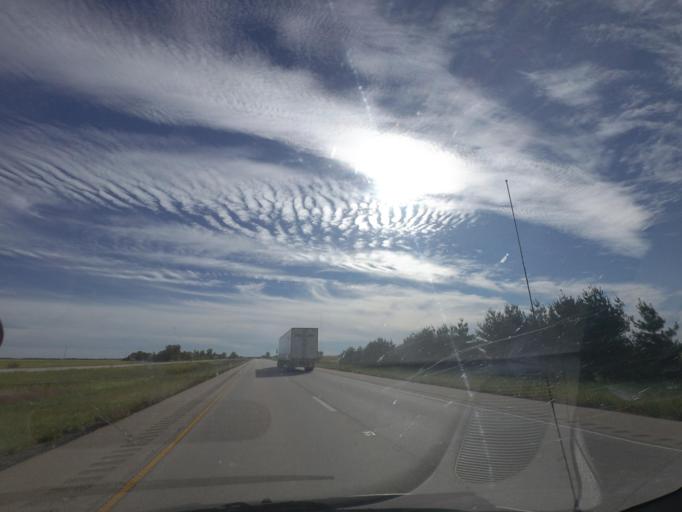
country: US
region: Illinois
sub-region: Piatt County
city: Cerro Gordo
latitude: 39.9694
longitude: -88.8121
